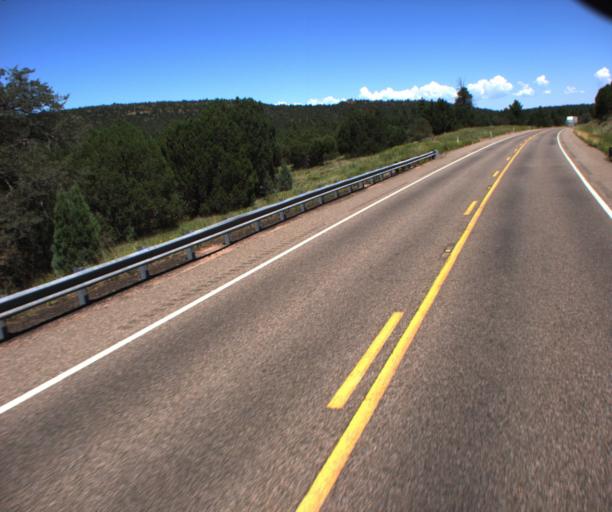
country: US
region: Arizona
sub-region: Gila County
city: San Carlos
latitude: 33.6782
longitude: -110.5729
